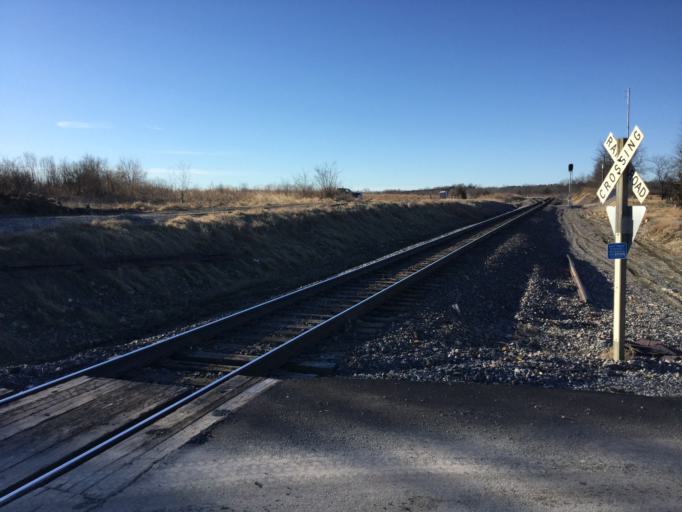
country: US
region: Kansas
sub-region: Linn County
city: Mound City
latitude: 38.2731
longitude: -94.9946
